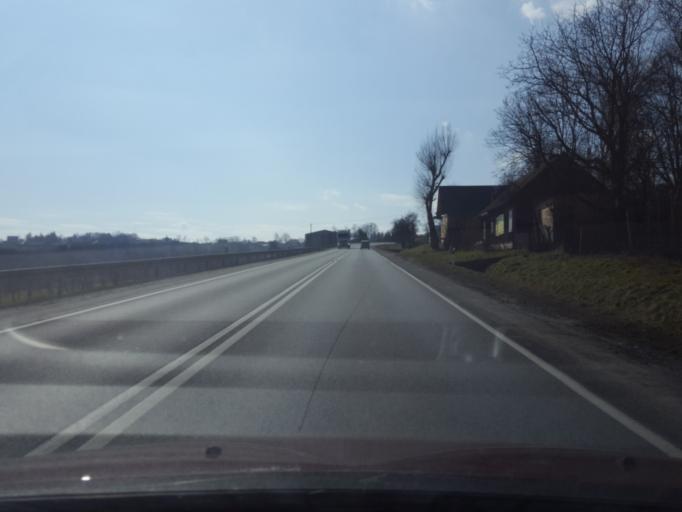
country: PL
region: Lesser Poland Voivodeship
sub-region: Powiat nowosadecki
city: Lososina Dolna
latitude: 49.7320
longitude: 20.6381
